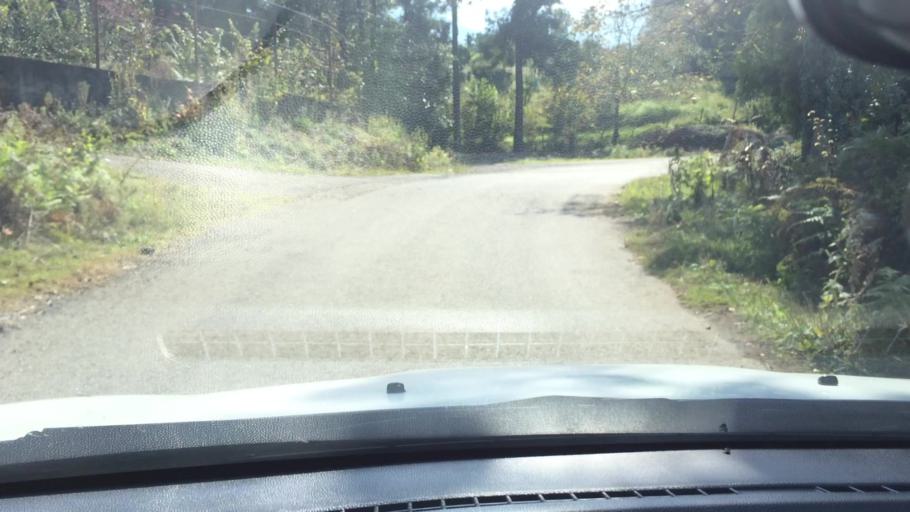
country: GE
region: Ajaria
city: Kobuleti
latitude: 41.8109
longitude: 41.8250
